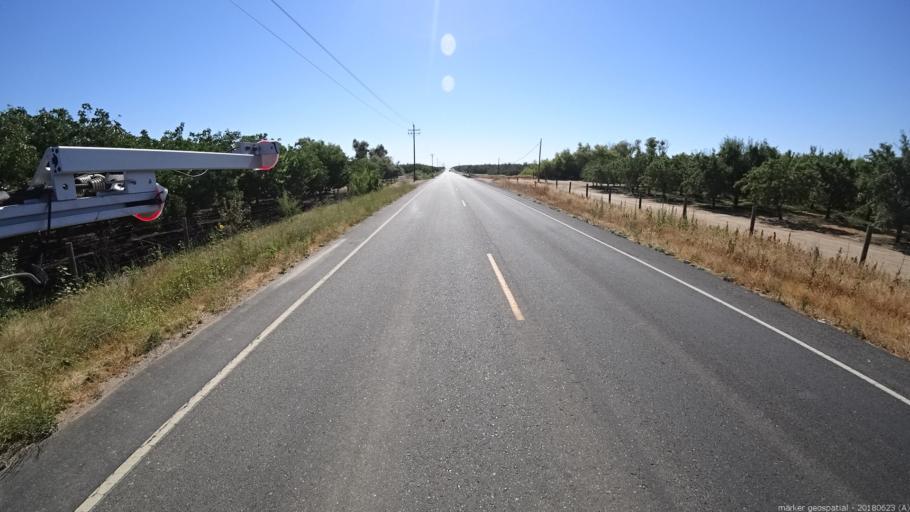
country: US
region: California
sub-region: Madera County
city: Parksdale
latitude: 36.9667
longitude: -119.9674
